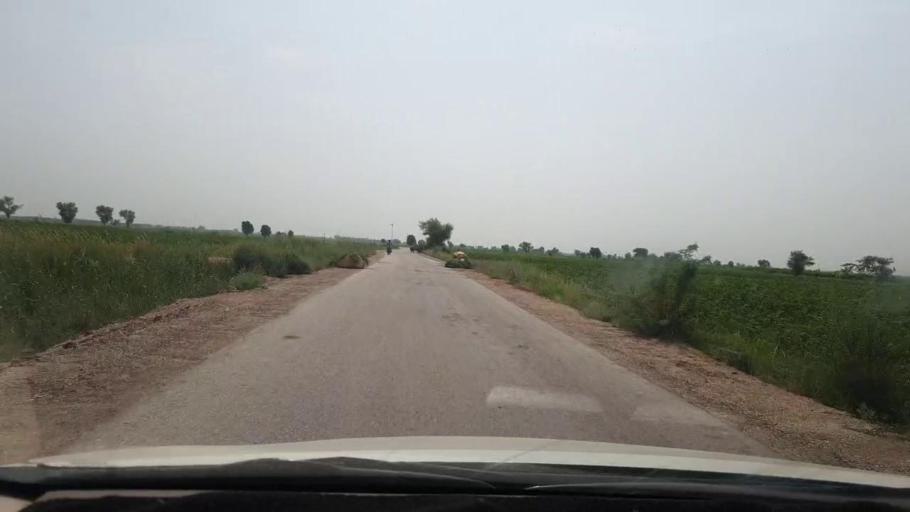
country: PK
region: Sindh
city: Rohri
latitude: 27.5378
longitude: 69.0016
